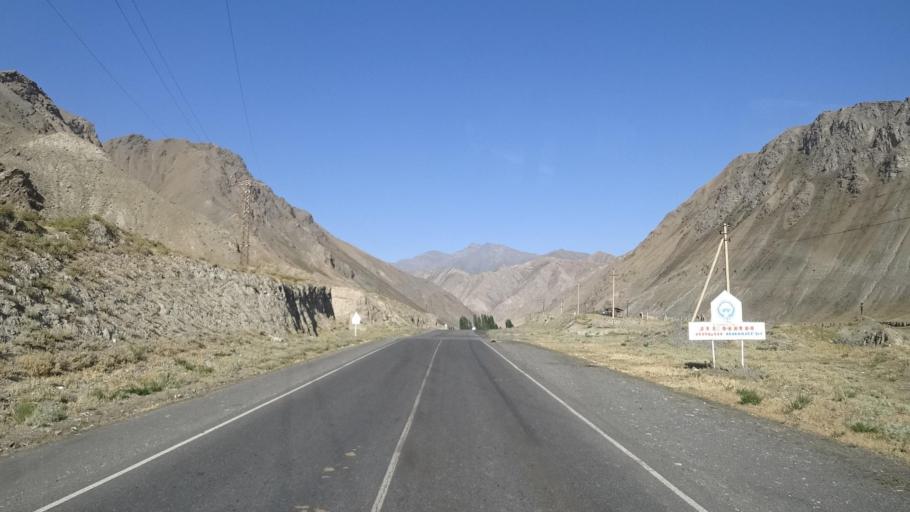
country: KG
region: Osh
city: Gul'cha
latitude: 40.0265
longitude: 73.4962
